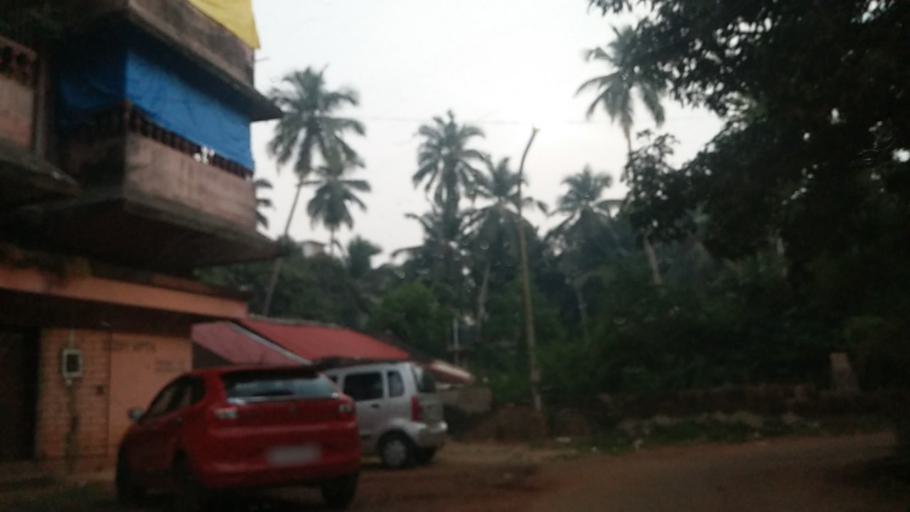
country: IN
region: Goa
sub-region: South Goa
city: Madgaon
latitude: 15.2846
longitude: 73.9551
